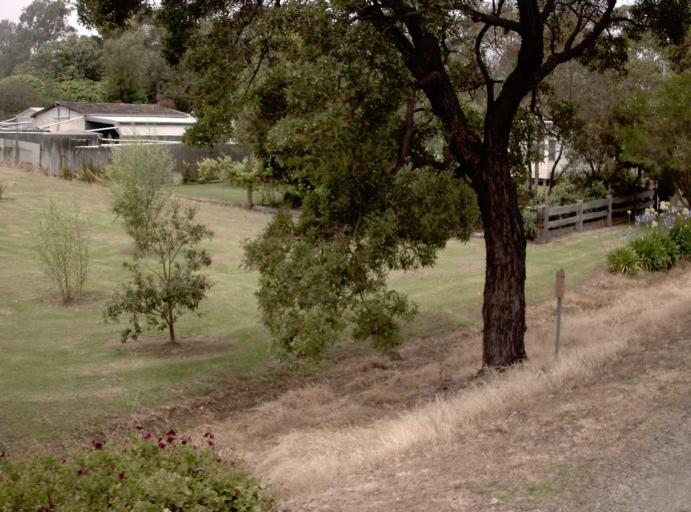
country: AU
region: Victoria
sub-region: Latrobe
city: Traralgon
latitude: -38.4723
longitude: 146.7172
